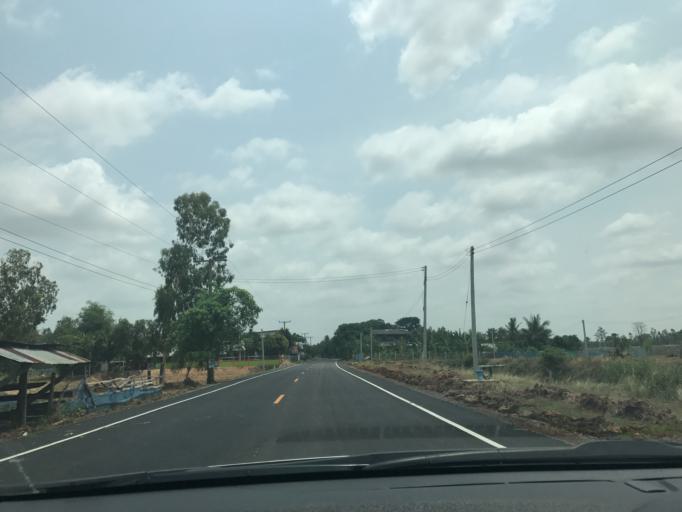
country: TH
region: Surin
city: Khwao Sinarin
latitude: 15.0432
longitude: 103.6507
